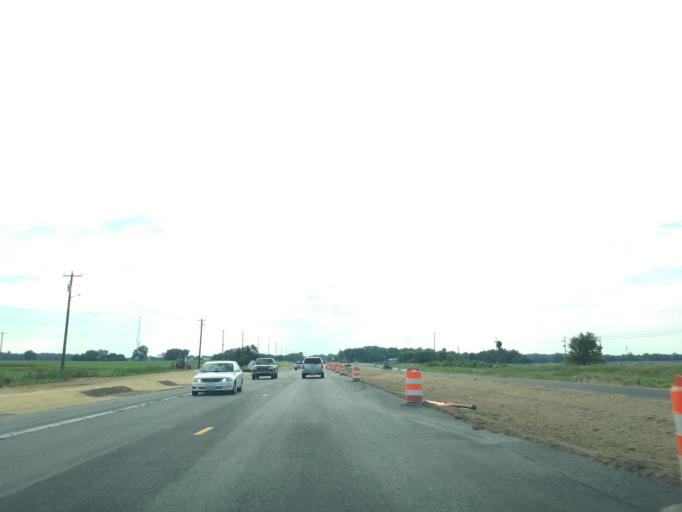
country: US
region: Maryland
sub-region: Queen Anne's County
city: Centreville
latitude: 38.9365
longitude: -76.0467
